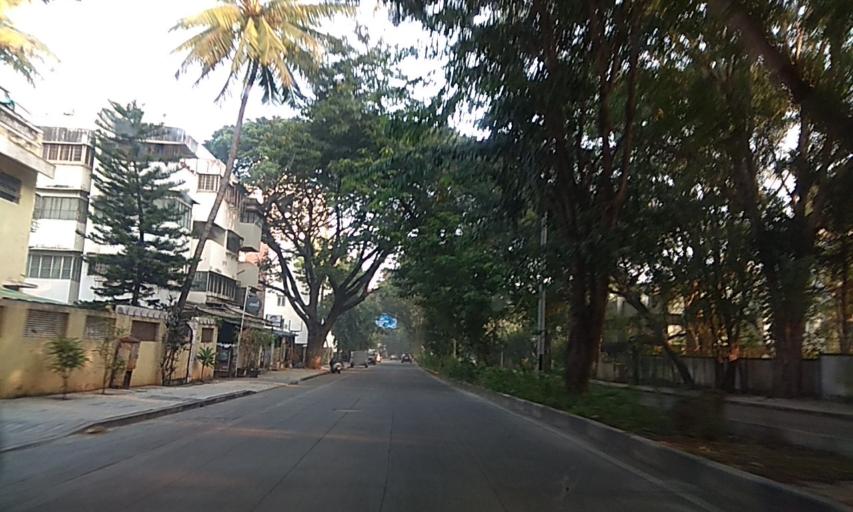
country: IN
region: Maharashtra
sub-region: Pune Division
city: Shivaji Nagar
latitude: 18.5446
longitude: 73.8172
